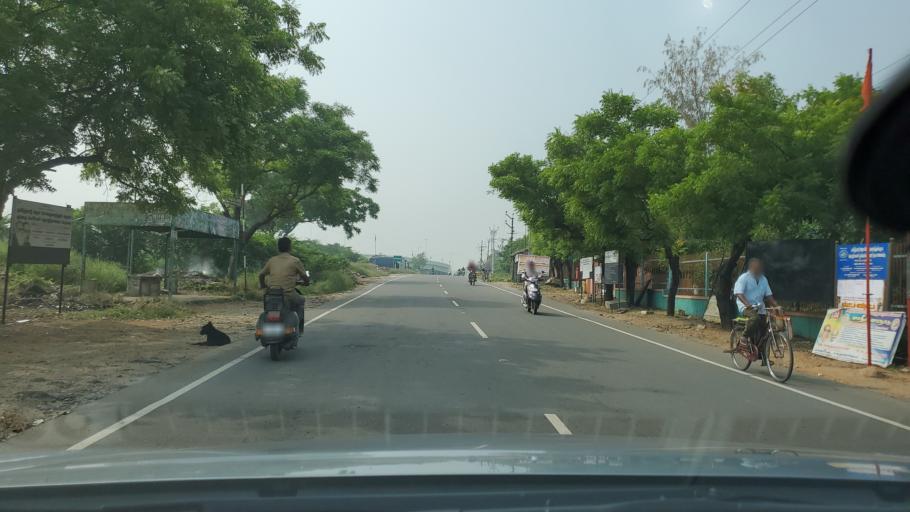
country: IN
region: Tamil Nadu
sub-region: Erode
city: Erode
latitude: 11.3208
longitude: 77.7141
